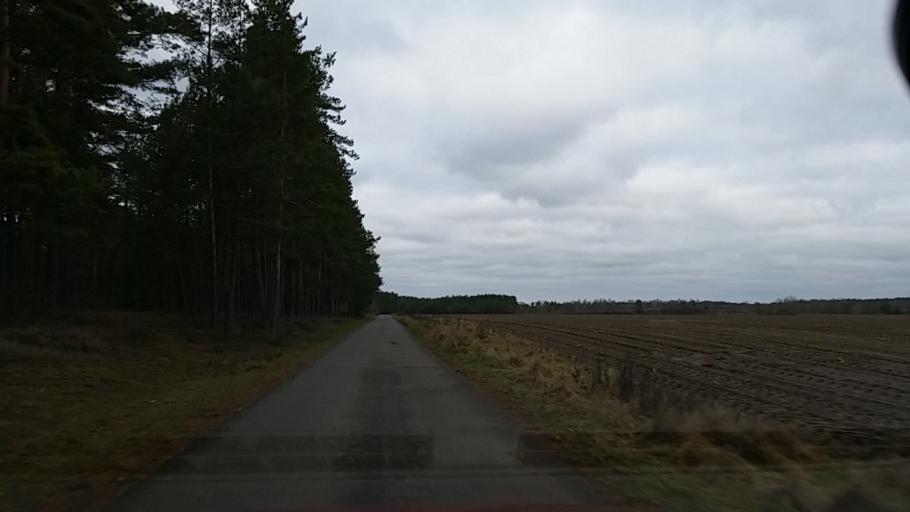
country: DE
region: Lower Saxony
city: Wieren
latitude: 52.8571
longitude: 10.6587
